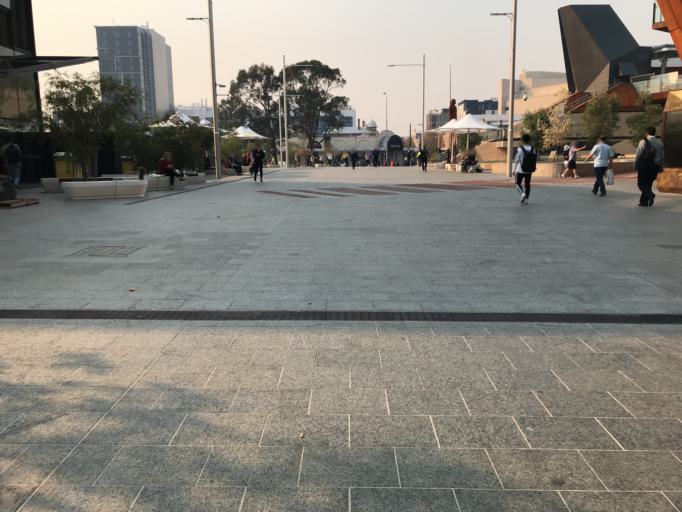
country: AU
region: Western Australia
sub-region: Cambridge
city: Perth
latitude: -31.9508
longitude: 115.8581
